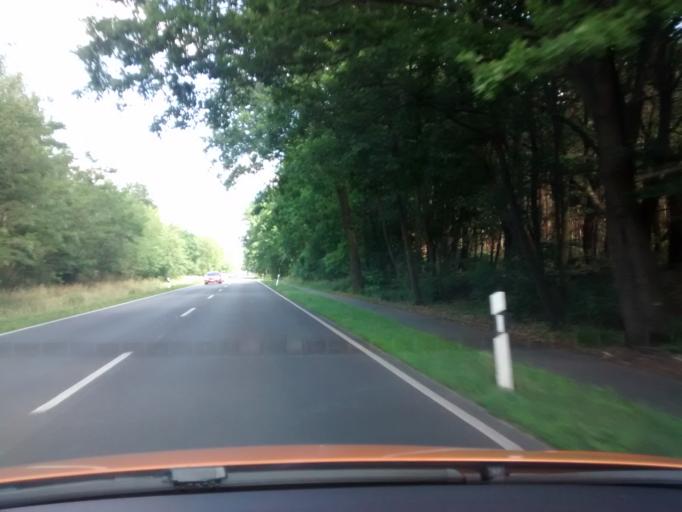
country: DE
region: Berlin
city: Kladow
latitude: 52.4642
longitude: 13.0832
